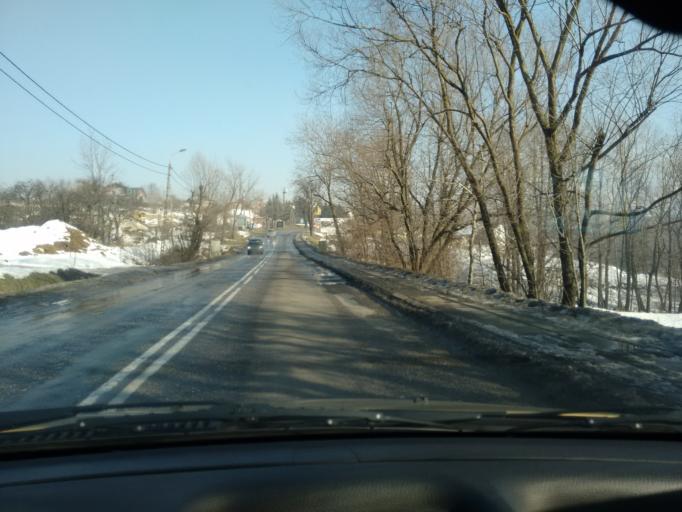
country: PL
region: Silesian Voivodeship
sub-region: Bielsko-Biala
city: Bielsko-Biala
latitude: 49.8261
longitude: 19.0990
